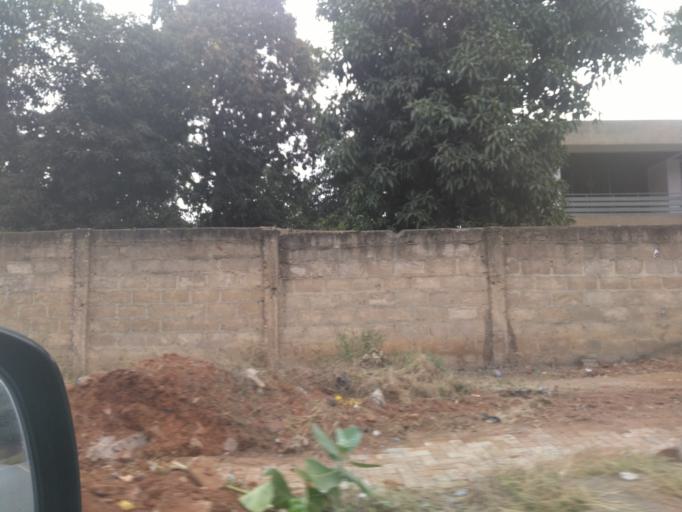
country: GH
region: Greater Accra
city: Accra
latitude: 5.6016
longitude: -0.1935
